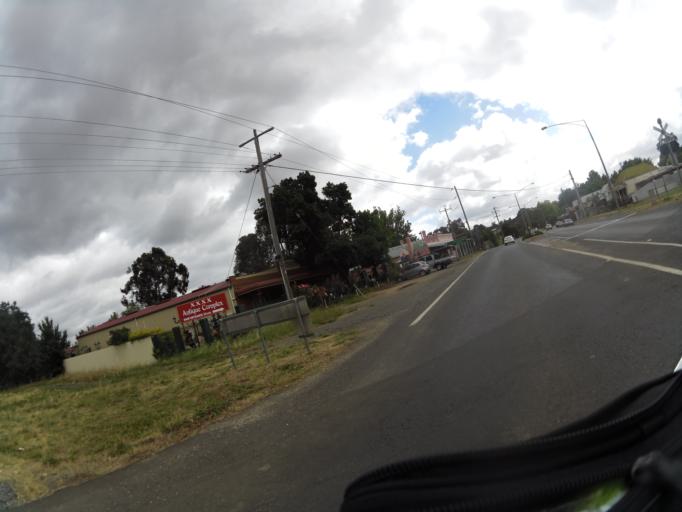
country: AU
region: Victoria
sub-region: Mount Alexander
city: Castlemaine
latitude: -37.0735
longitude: 144.2061
